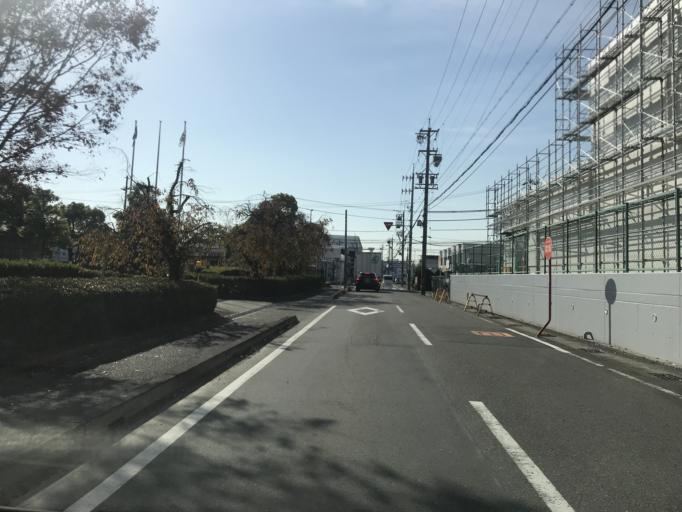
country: JP
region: Aichi
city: Iwakura
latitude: 35.2300
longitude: 136.8546
